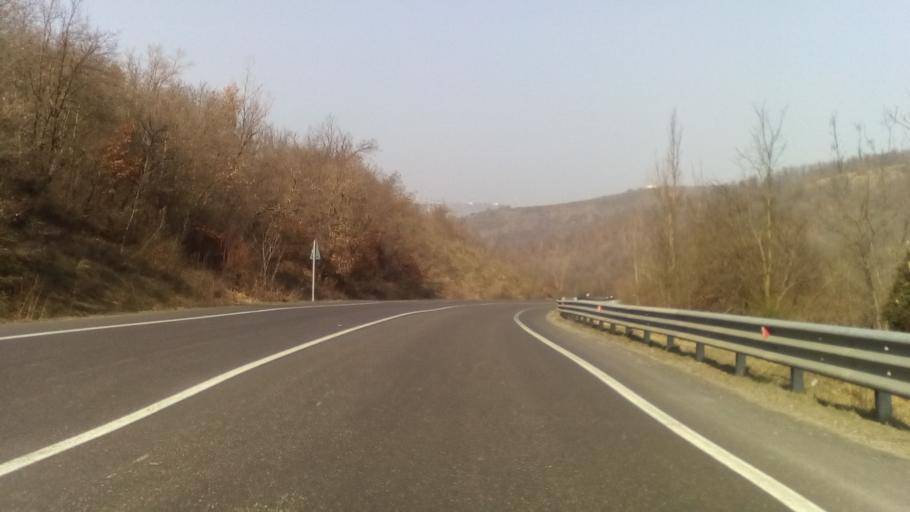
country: IT
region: Emilia-Romagna
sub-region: Provincia di Modena
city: Serramazzoni
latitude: 44.4477
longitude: 10.8341
